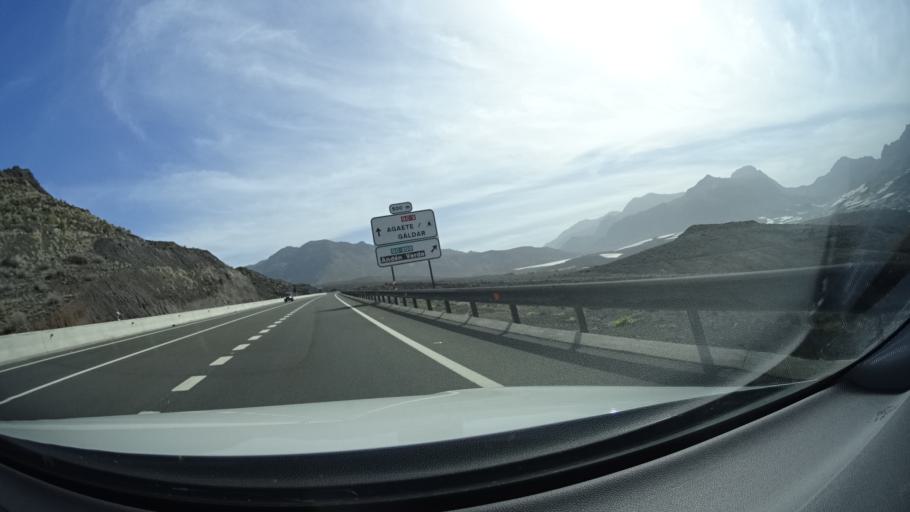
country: ES
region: Canary Islands
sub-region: Provincia de Las Palmas
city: San Nicolas
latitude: 28.0079
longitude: -15.7971
